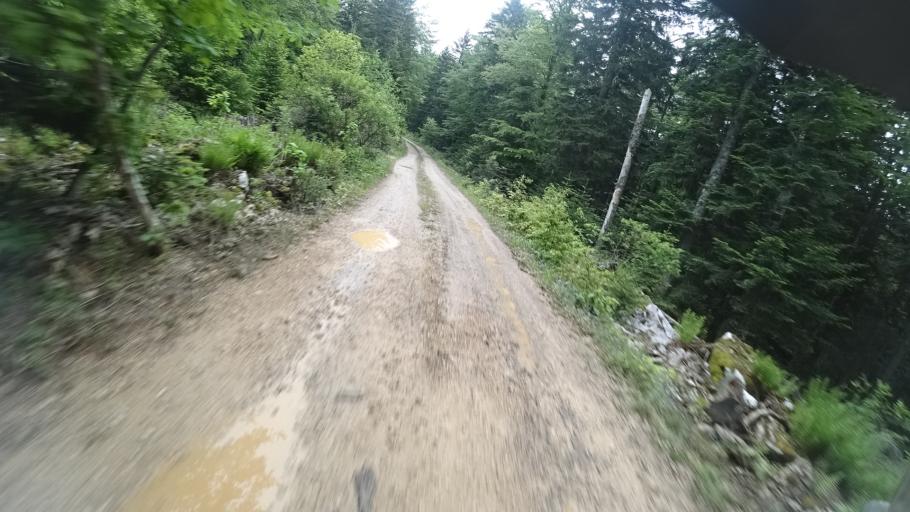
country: BA
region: Federation of Bosnia and Herzegovina
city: Bihac
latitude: 44.7015
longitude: 15.8309
